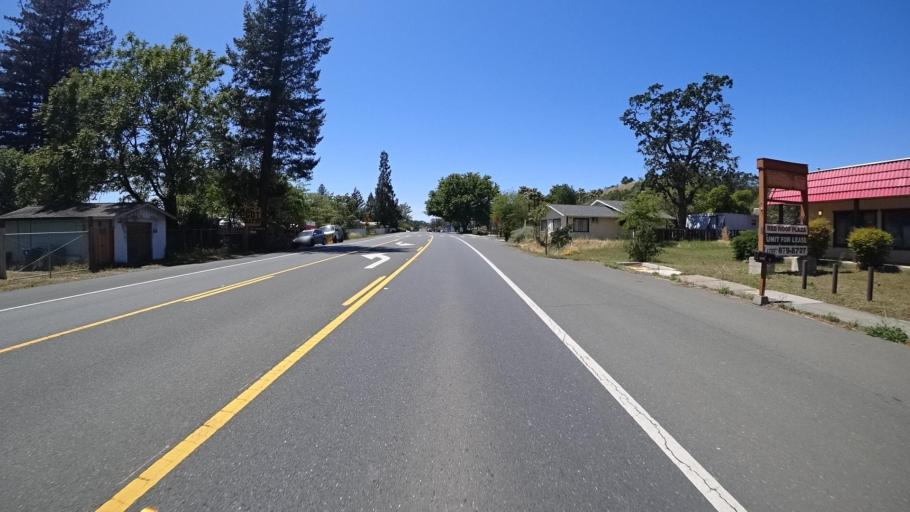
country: US
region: California
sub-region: Lake County
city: Nice
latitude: 39.1230
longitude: -122.8448
